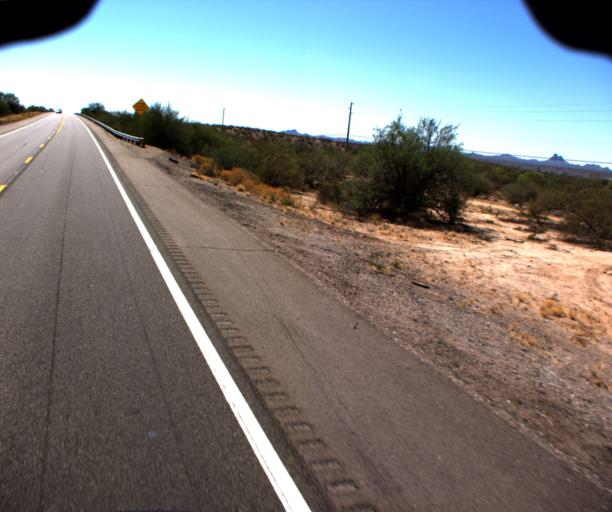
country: US
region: Arizona
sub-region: Maricopa County
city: Wickenburg
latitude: 34.0332
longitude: -112.8211
